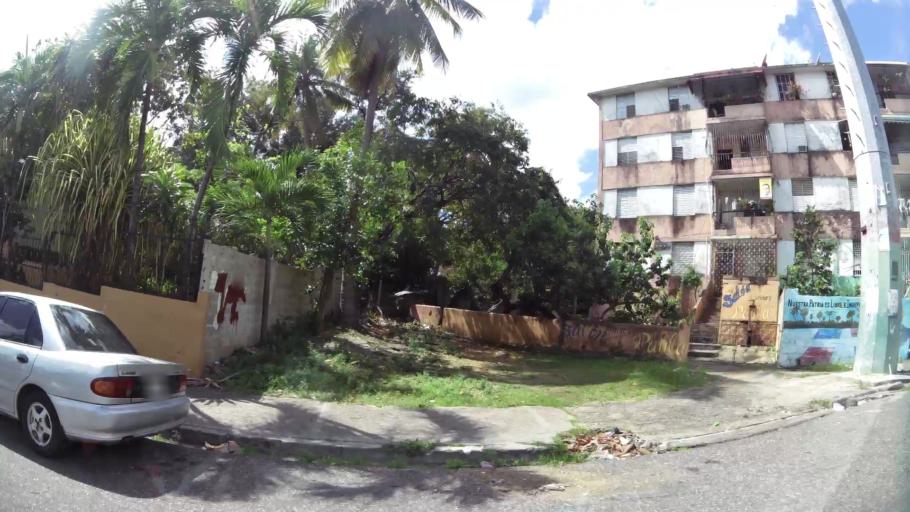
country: DO
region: Nacional
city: San Carlos
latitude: 18.4885
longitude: -69.8857
